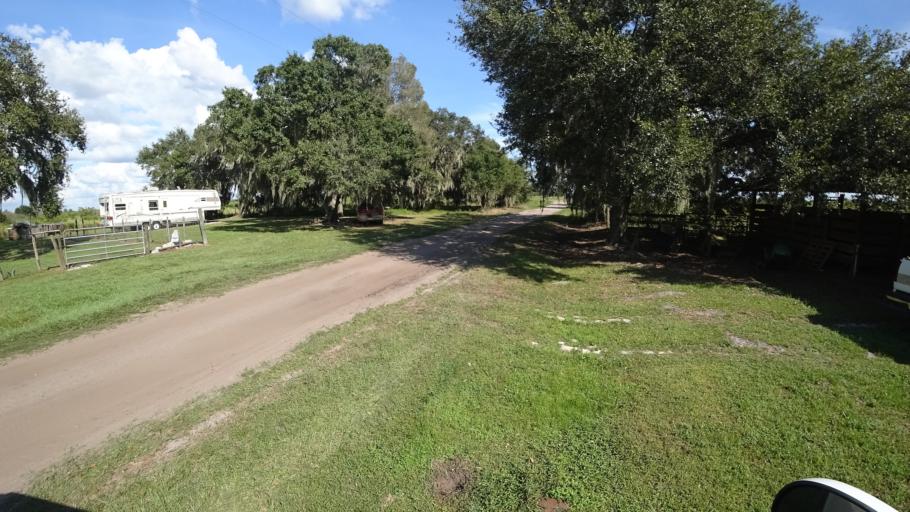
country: US
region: Florida
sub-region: DeSoto County
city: Arcadia
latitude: 27.3092
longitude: -82.0925
